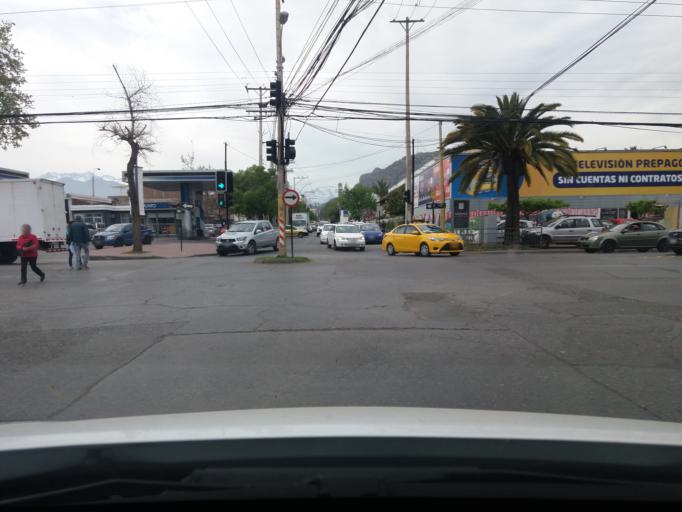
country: CL
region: Valparaiso
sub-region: Provincia de Los Andes
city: Los Andes
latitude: -32.8318
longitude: -70.6026
